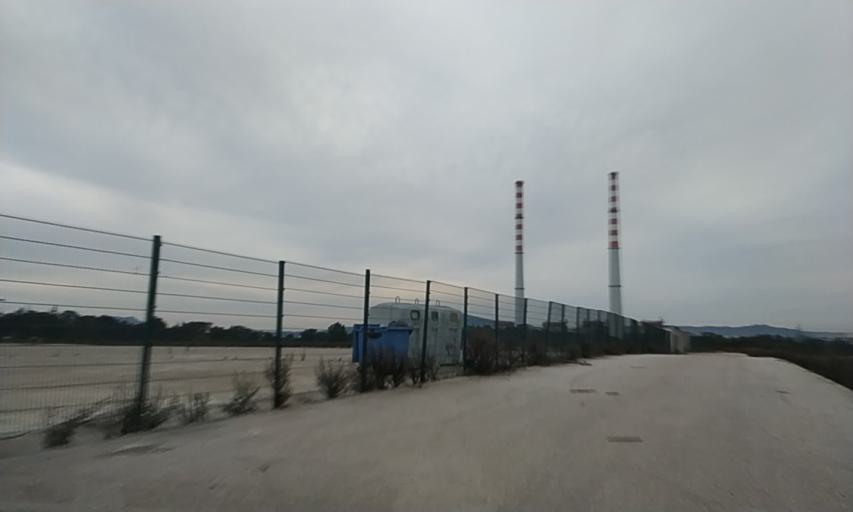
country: PT
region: Setubal
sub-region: Setubal
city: Setubal
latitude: 38.5064
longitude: -8.8366
